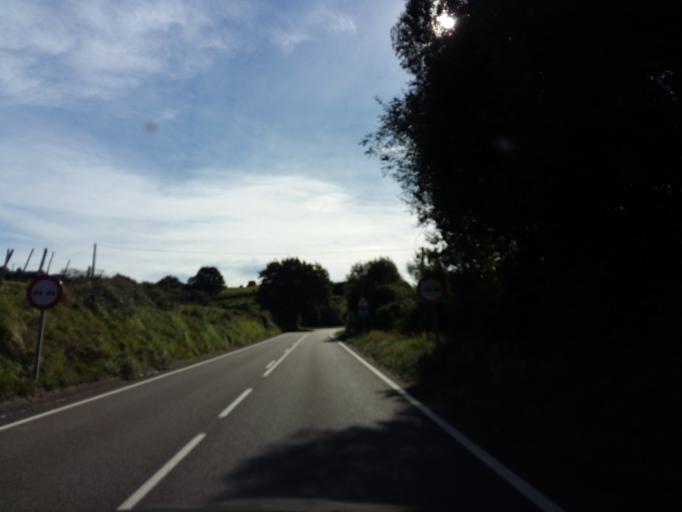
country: ES
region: Cantabria
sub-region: Provincia de Cantabria
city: San Vicente de la Barquera
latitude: 43.3459
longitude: -4.4871
